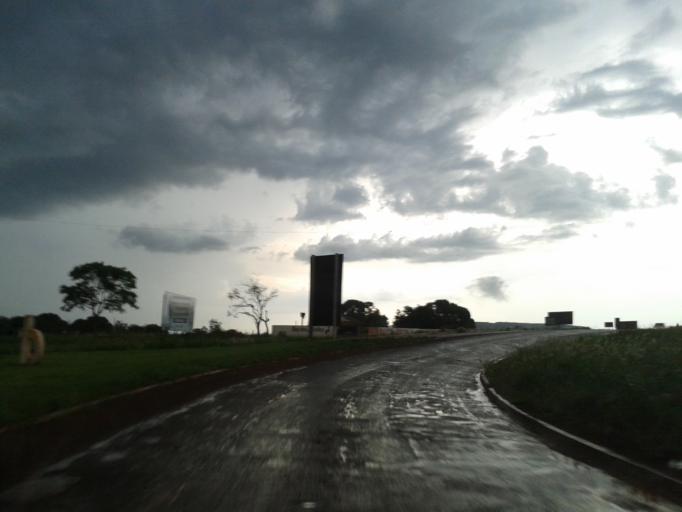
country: BR
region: Goias
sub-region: Quirinopolis
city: Quirinopolis
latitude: -18.4382
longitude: -50.4175
